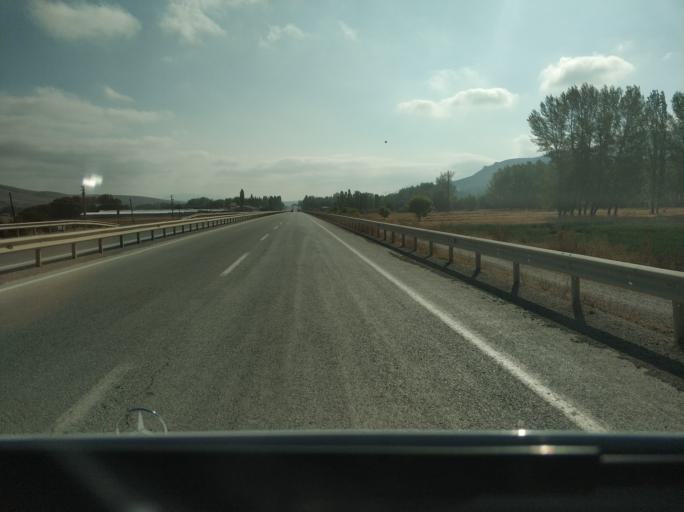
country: TR
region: Sivas
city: Yildizeli
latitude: 39.8382
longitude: 36.4553
